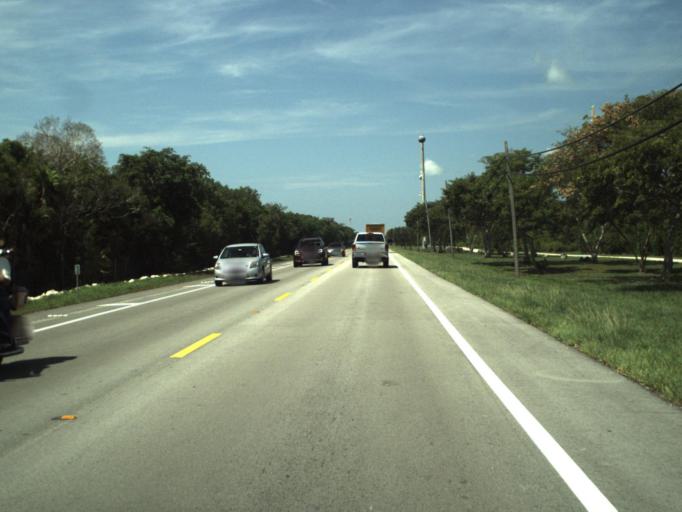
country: US
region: Florida
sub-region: Monroe County
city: Marathon
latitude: 24.7408
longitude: -80.9979
